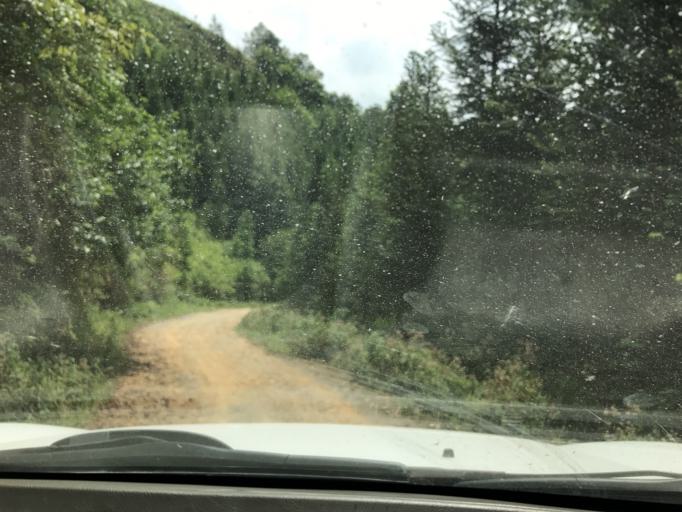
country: CN
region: Guangxi Zhuangzu Zizhiqu
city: Xinzhou
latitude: 24.9859
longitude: 105.9373
